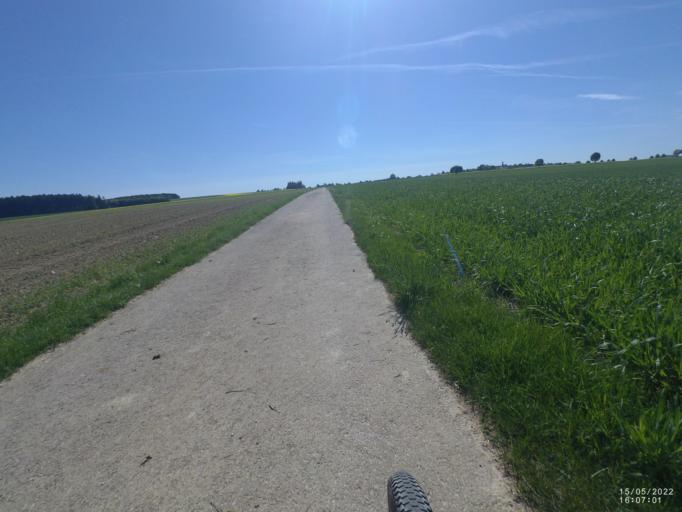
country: DE
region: Baden-Wuerttemberg
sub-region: Regierungsbezirk Stuttgart
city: Bolheim
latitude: 48.6015
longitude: 10.1505
